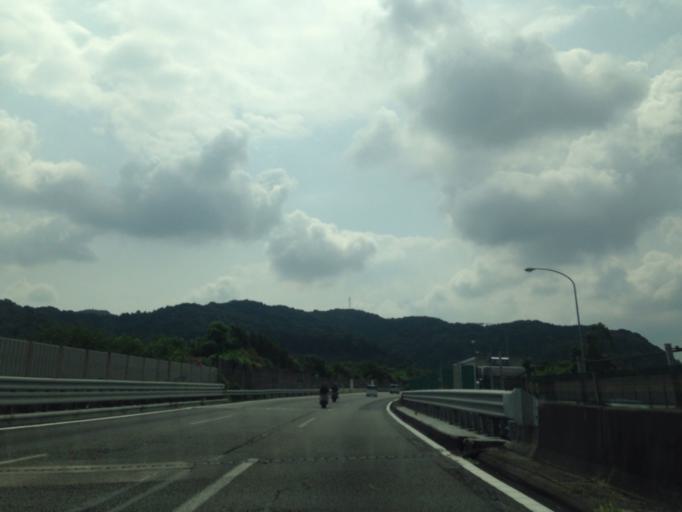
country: JP
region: Aichi
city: Gamagori
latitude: 34.8916
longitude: 137.2628
